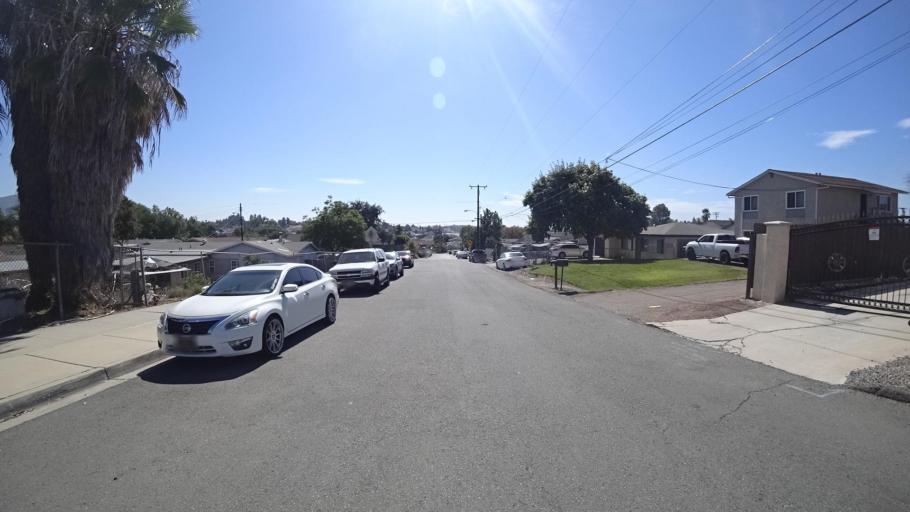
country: US
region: California
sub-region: San Diego County
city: La Presa
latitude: 32.7114
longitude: -117.0060
